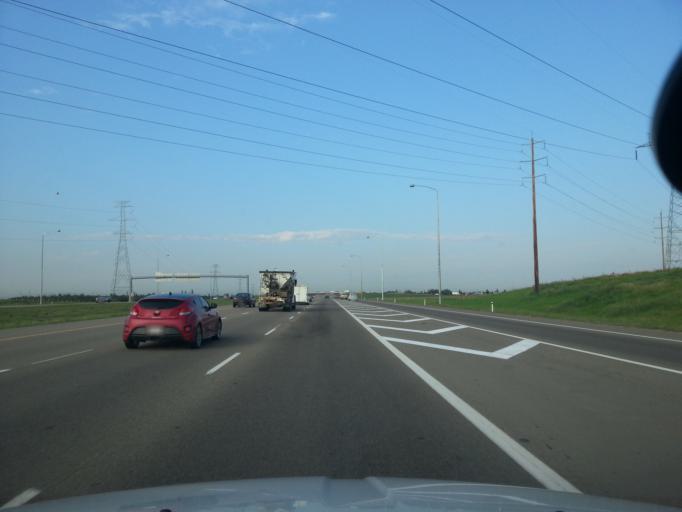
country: CA
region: Alberta
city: St. Albert
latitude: 53.6142
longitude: -113.6063
